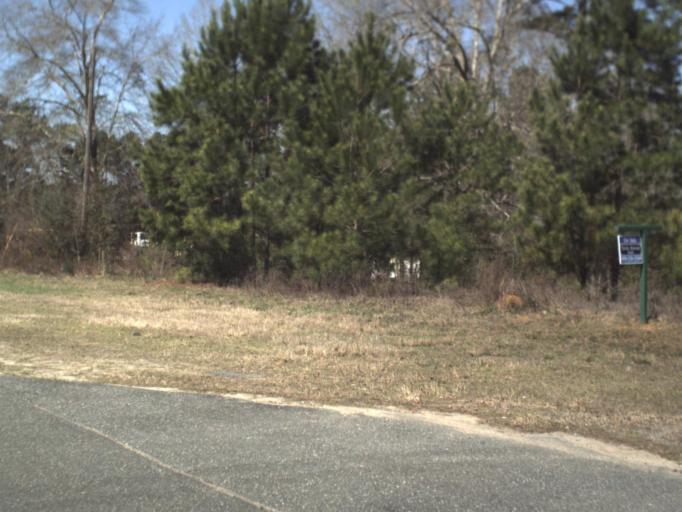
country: US
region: Florida
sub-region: Jackson County
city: Marianna
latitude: 30.7840
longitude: -85.2641
